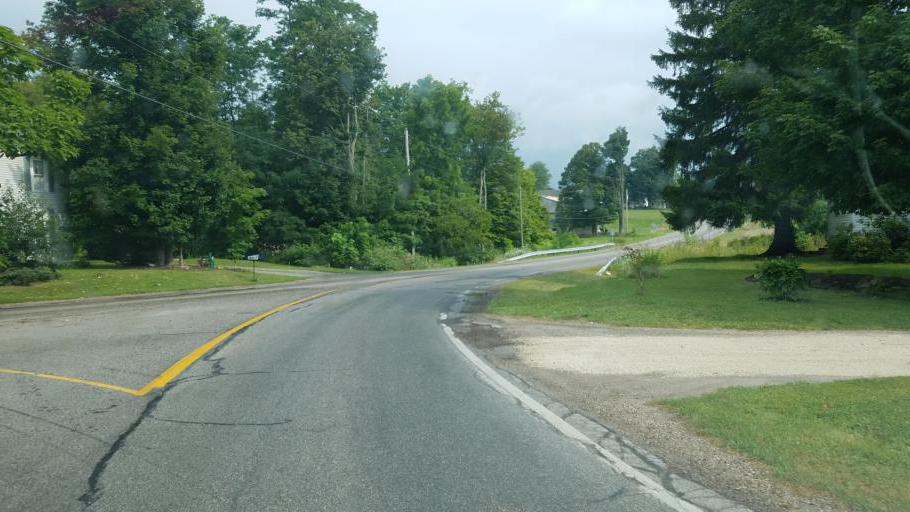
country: US
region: Ohio
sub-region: Ashtabula County
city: Orwell
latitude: 41.4631
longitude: -80.9543
